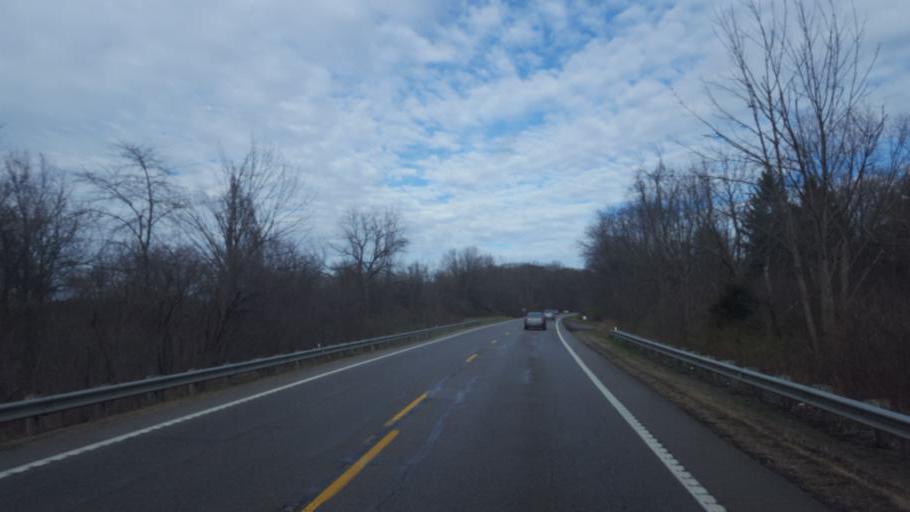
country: US
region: Ohio
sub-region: Delaware County
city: Sunbury
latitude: 40.2504
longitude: -82.8556
